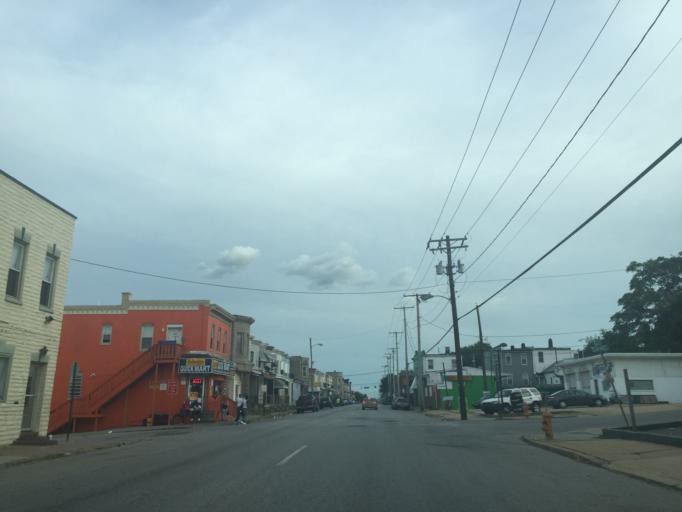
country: US
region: Maryland
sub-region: Anne Arundel County
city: Brooklyn Park
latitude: 39.2248
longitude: -76.5885
